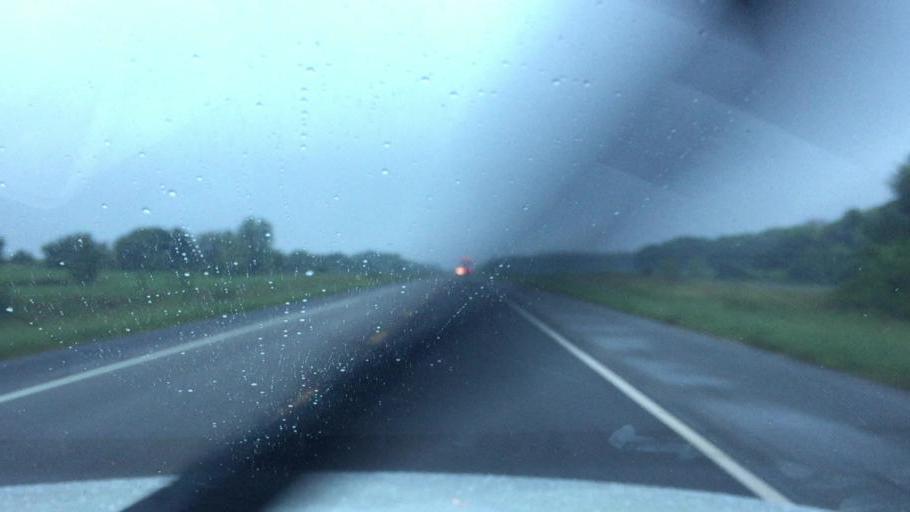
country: US
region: Kansas
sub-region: Montgomery County
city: Cherryvale
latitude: 37.4259
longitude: -95.4924
